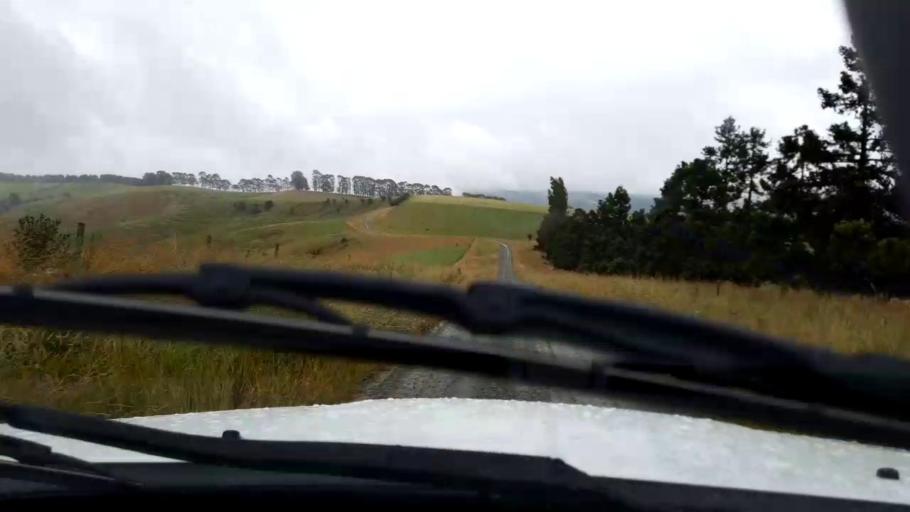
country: NZ
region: Canterbury
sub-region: Timaru District
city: Pleasant Point
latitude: -44.1763
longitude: 171.1149
